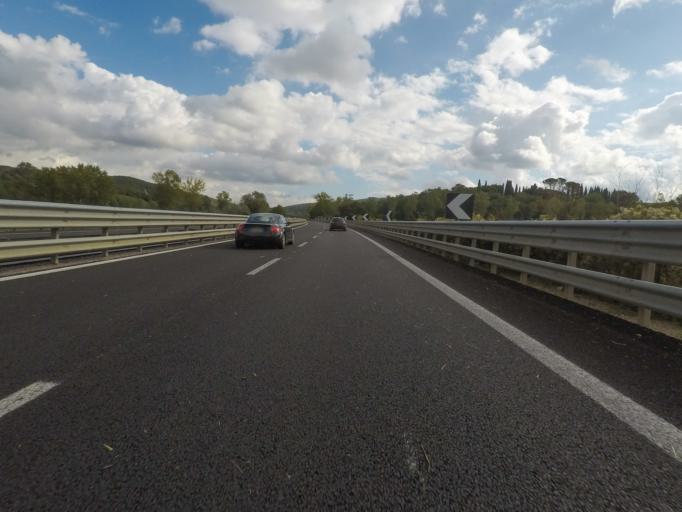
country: IT
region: Tuscany
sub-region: Provincia di Siena
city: Serre di Rapolano
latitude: 43.2466
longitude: 11.6518
